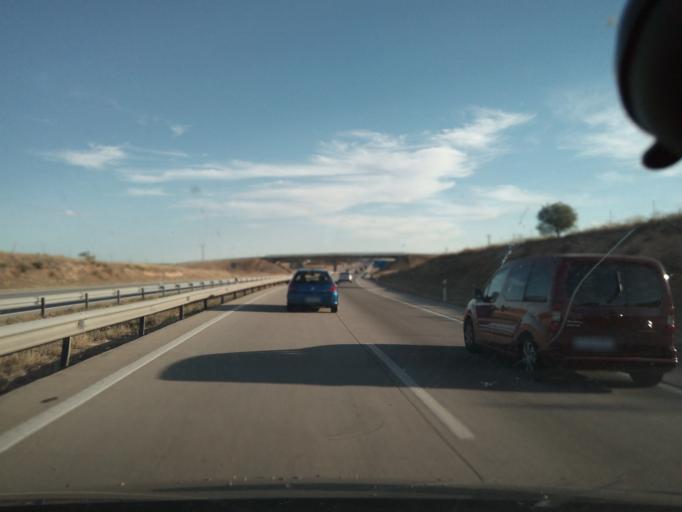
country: ES
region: Castille-La Mancha
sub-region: Province of Toledo
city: Dosbarrios
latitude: 39.8845
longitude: -3.4710
